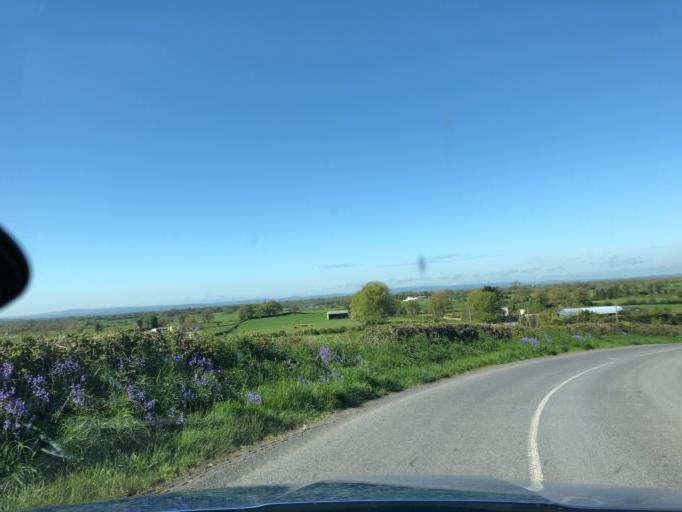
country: IE
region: Connaught
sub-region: County Galway
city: Portumna
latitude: 53.1677
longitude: -8.2128
